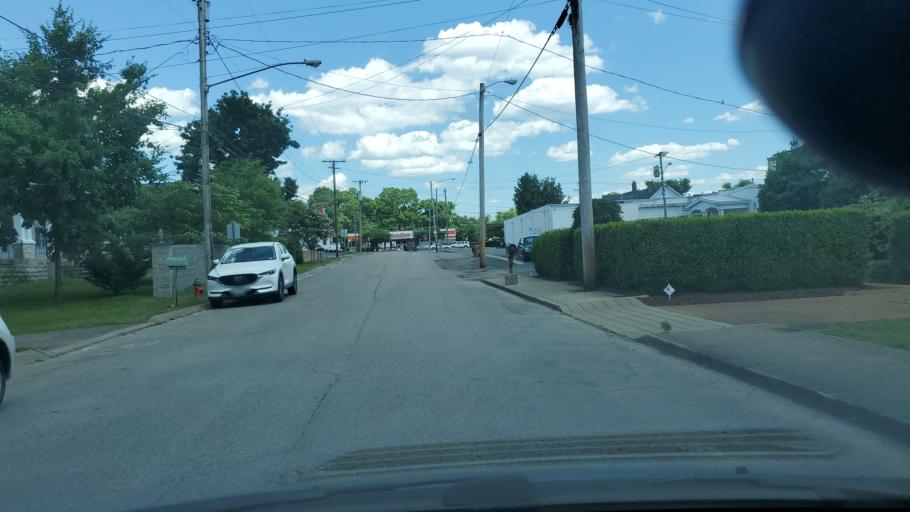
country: US
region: Tennessee
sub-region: Davidson County
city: Nashville
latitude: 36.2006
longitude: -86.7420
